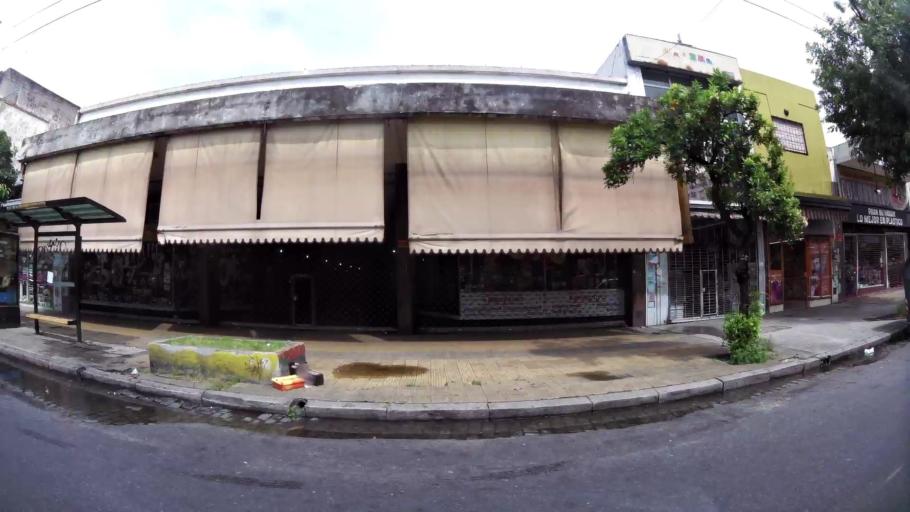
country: AR
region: Buenos Aires
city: Caseros
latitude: -34.6144
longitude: -58.5256
